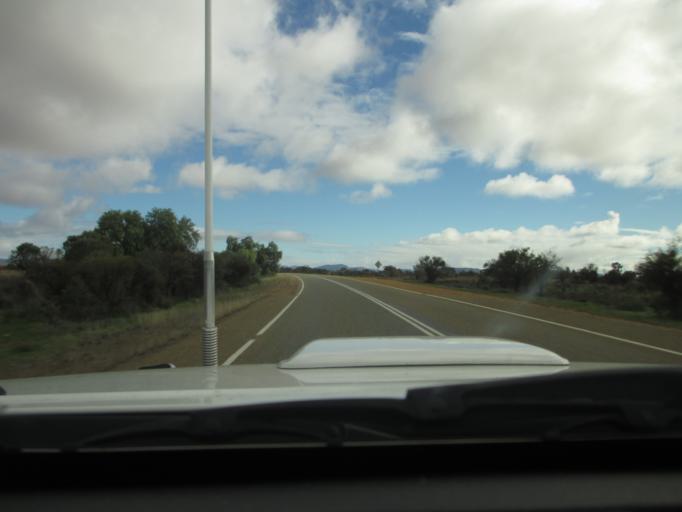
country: AU
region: South Australia
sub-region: Flinders Ranges
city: Quorn
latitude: -32.0756
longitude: 138.5003
